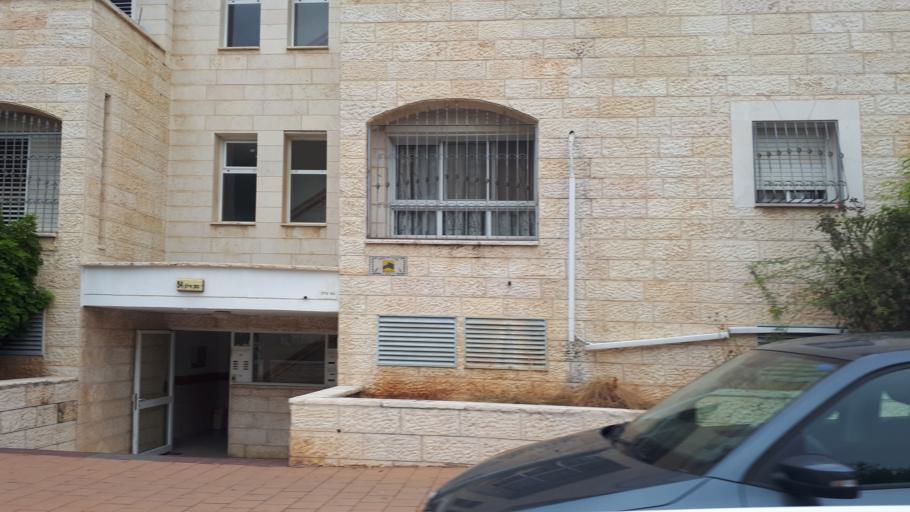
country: IL
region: Central District
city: Modiin
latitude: 31.9027
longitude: 35.0113
